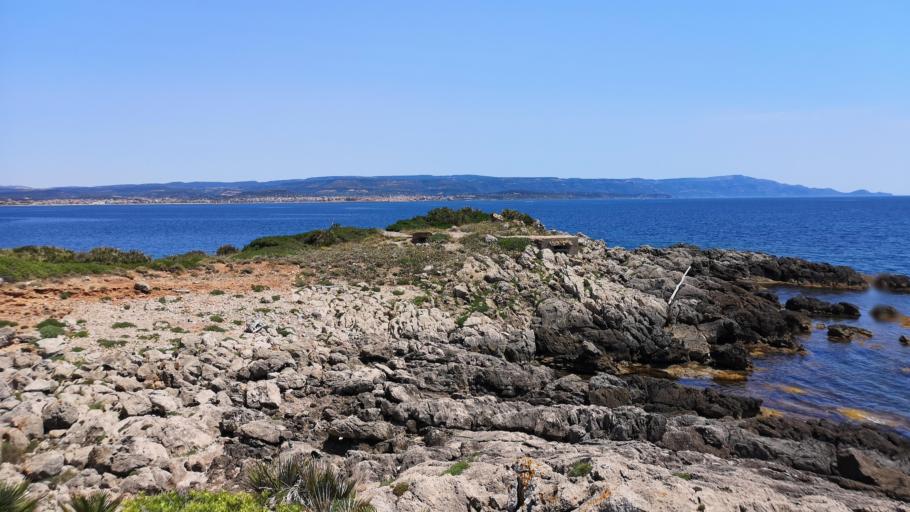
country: IT
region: Sardinia
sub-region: Provincia di Sassari
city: Alghero
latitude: 40.5818
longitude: 8.2647
